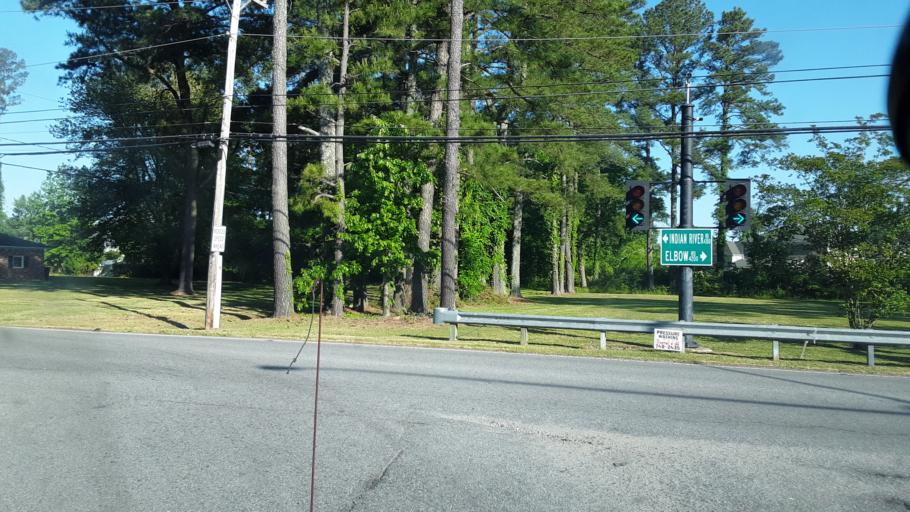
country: US
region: Virginia
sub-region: City of Chesapeake
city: Chesapeake
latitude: 36.7614
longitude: -76.1400
